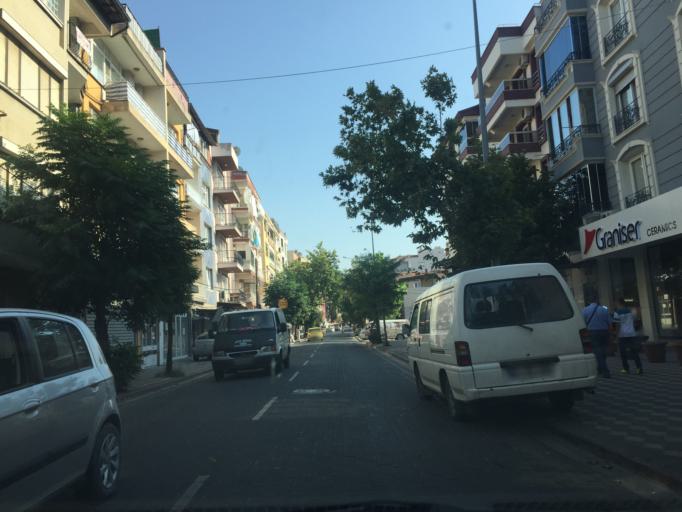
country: TR
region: Manisa
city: Akhisar
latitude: 38.9160
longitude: 27.8418
